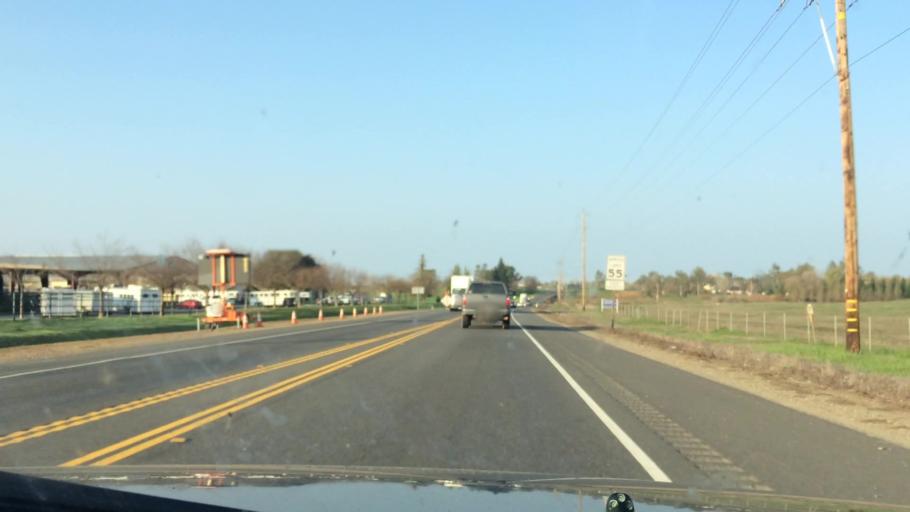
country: US
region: California
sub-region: Sacramento County
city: Rancho Murieta
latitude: 38.4975
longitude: -121.1043
